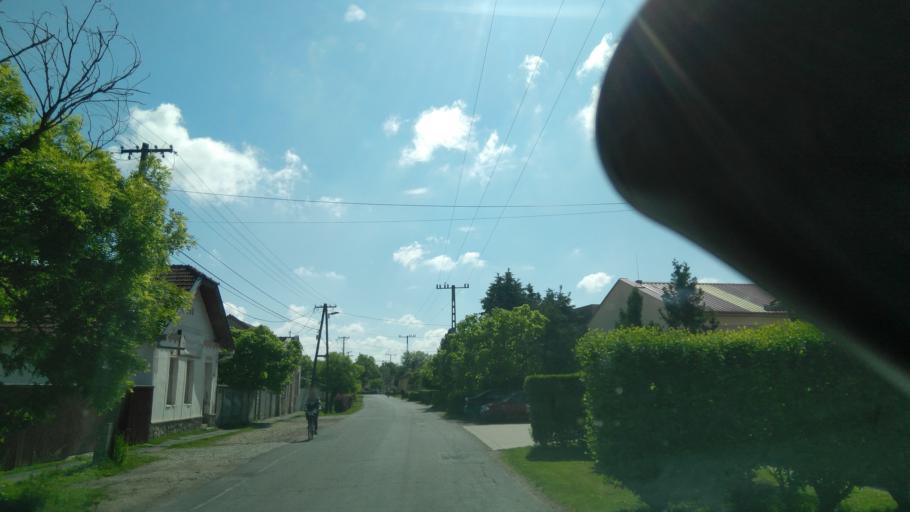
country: HU
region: Bekes
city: Bekes
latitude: 46.7762
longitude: 21.1236
